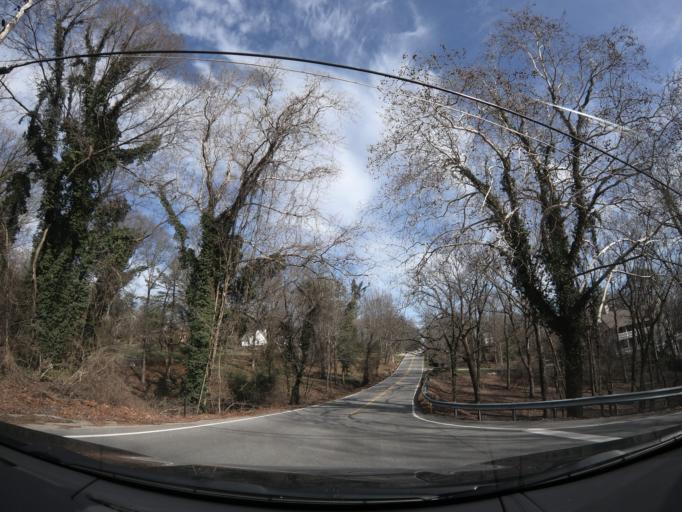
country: US
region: Tennessee
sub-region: Hamilton County
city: Lookout Mountain
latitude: 34.9939
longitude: -85.3472
